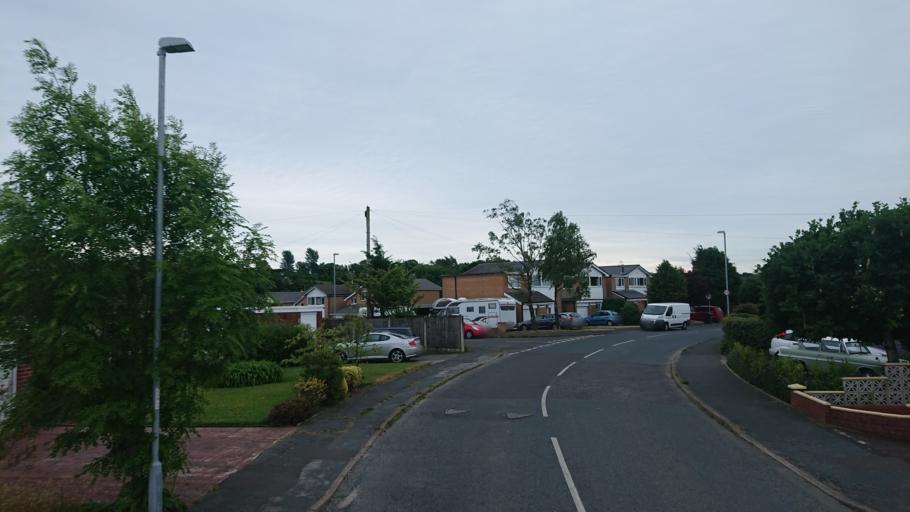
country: GB
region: England
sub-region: Lancashire
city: Lancaster
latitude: 54.0276
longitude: -2.7853
